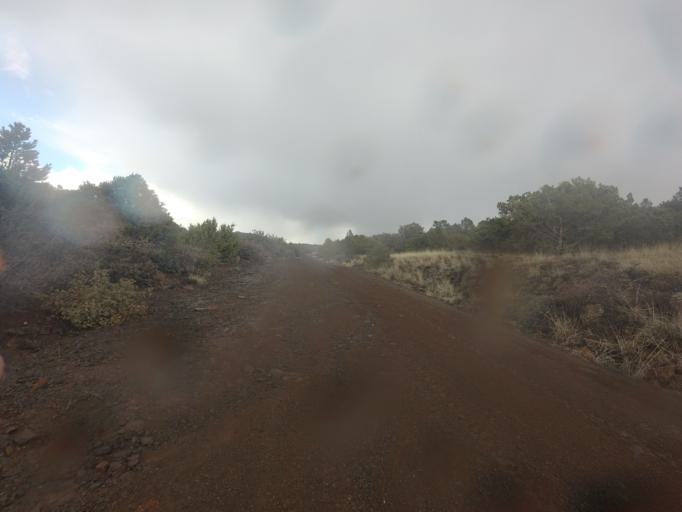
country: US
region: Arizona
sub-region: Gila County
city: Pine
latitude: 34.4037
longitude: -111.5694
